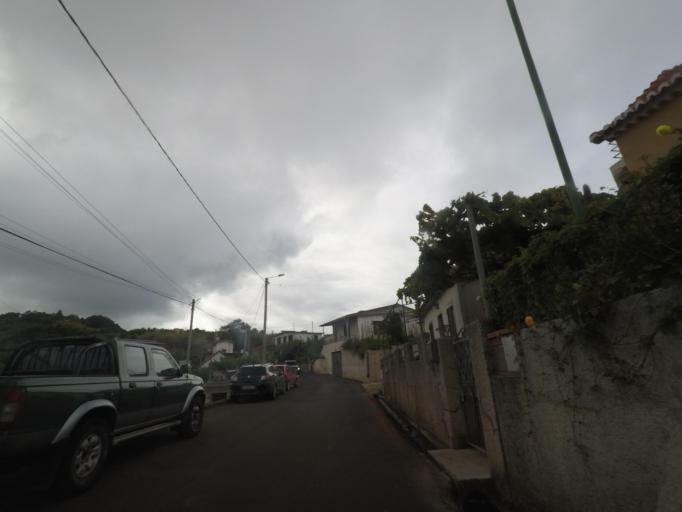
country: PT
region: Madeira
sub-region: Santana
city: Santana
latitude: 32.8311
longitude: -16.9102
